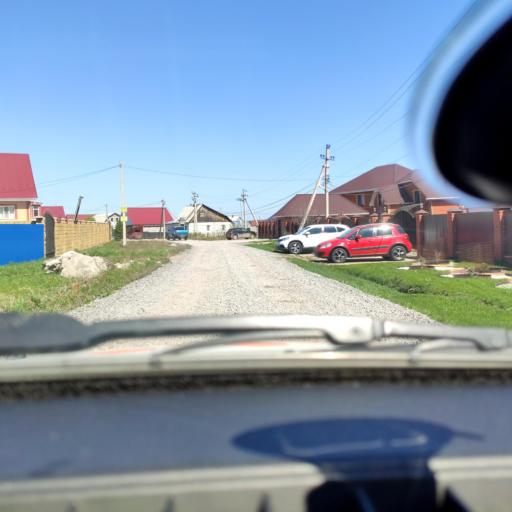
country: RU
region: Bashkortostan
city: Iglino
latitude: 54.7946
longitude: 56.2792
